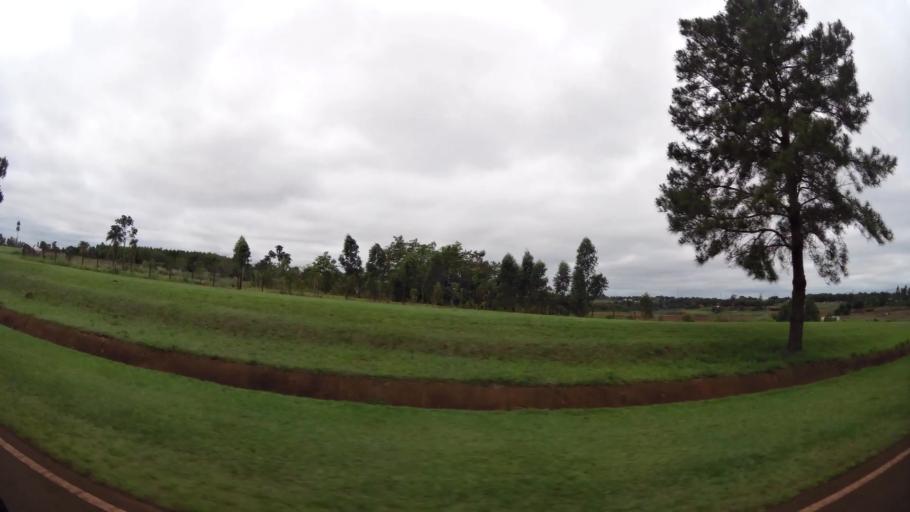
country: PY
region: Alto Parana
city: Colonia Yguazu
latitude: -25.4778
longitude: -54.8609
